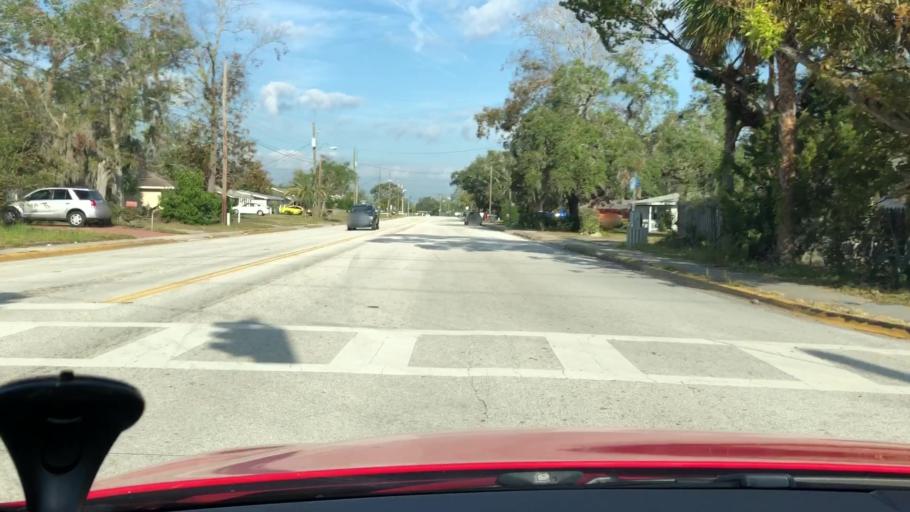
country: US
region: Florida
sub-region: Volusia County
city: Daytona Beach
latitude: 29.2143
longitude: -81.0526
